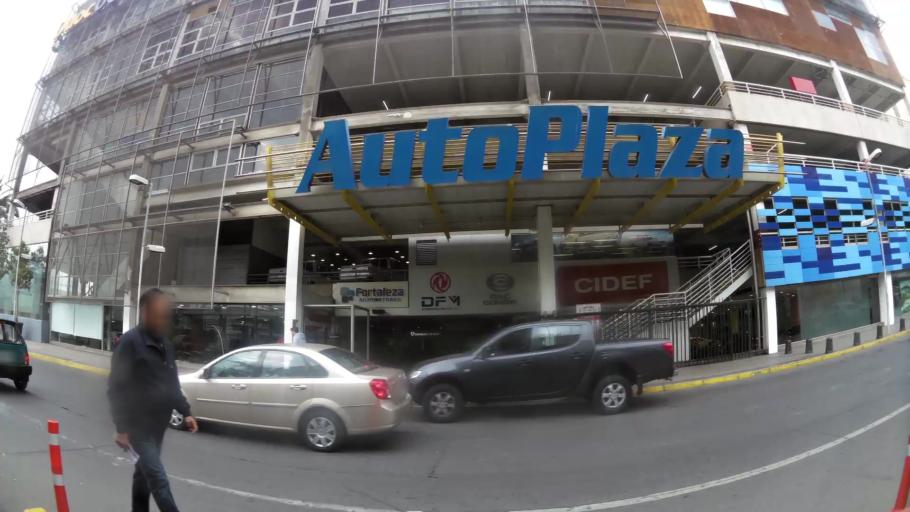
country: CL
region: Santiago Metropolitan
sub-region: Provincia de Santiago
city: Villa Presidente Frei, Nunoa, Santiago, Chile
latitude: -33.5160
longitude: -70.5985
